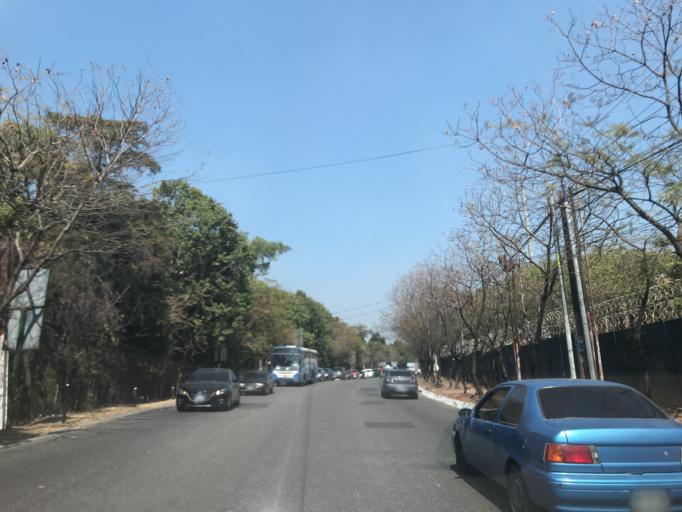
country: GT
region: Guatemala
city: Villa Nueva
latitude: 14.5348
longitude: -90.5567
